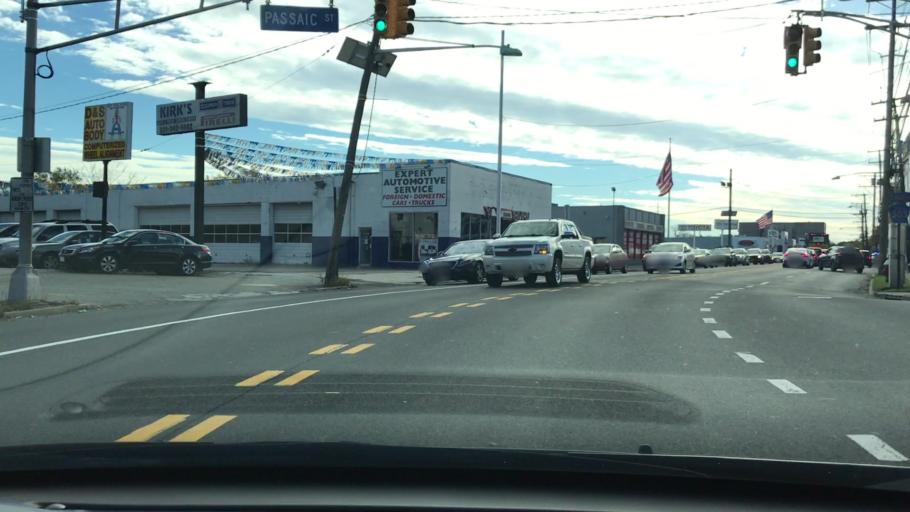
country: US
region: New Jersey
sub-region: Bergen County
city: Hackensack
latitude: 40.8890
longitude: -74.0386
